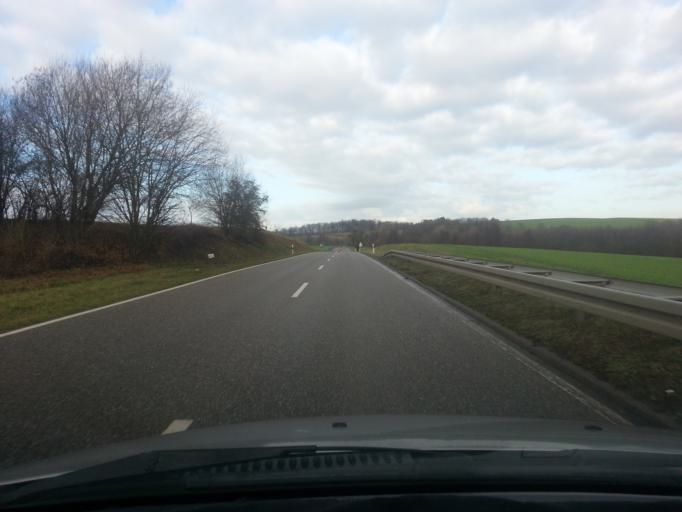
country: DE
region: Baden-Wuerttemberg
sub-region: Regierungsbezirk Stuttgart
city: Eppingen
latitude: 49.1467
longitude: 8.8940
